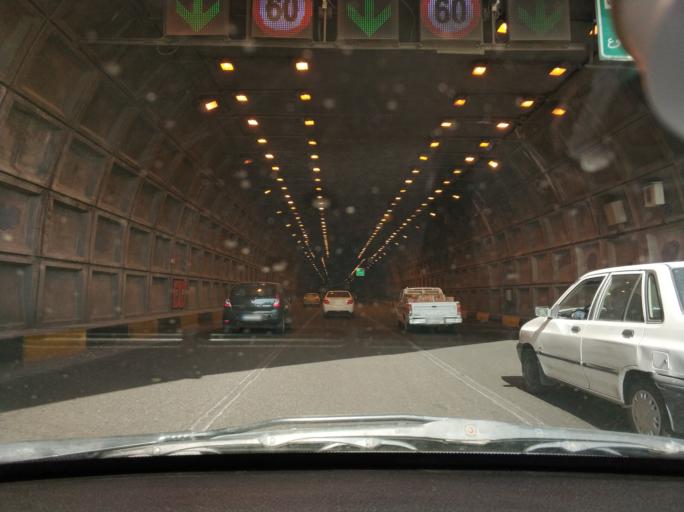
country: IR
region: Tehran
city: Tehran
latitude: 35.7409
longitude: 51.4158
